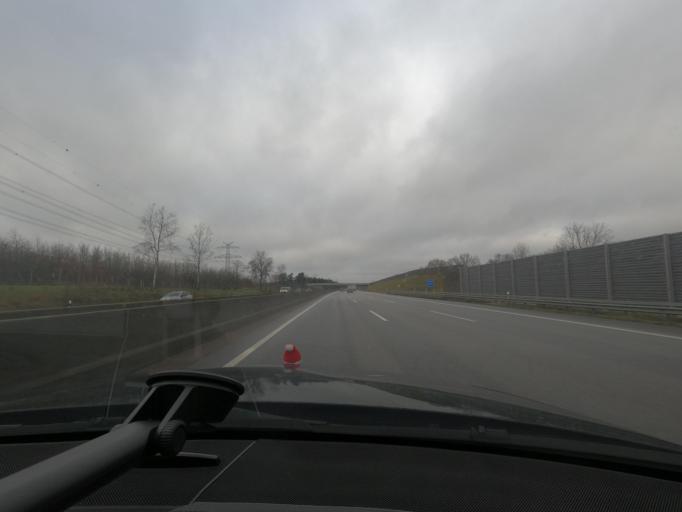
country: DE
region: Schleswig-Holstein
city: Kaltenkirchen
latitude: 53.8221
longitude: 9.9232
